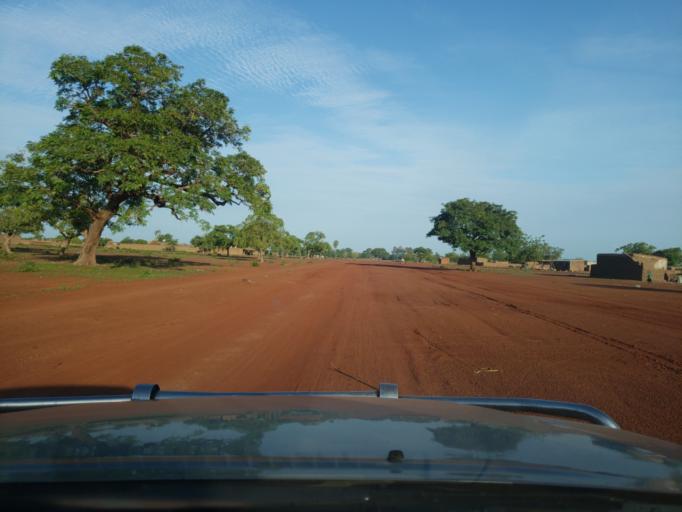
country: ML
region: Sikasso
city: Koutiala
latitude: 12.4047
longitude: -5.5334
